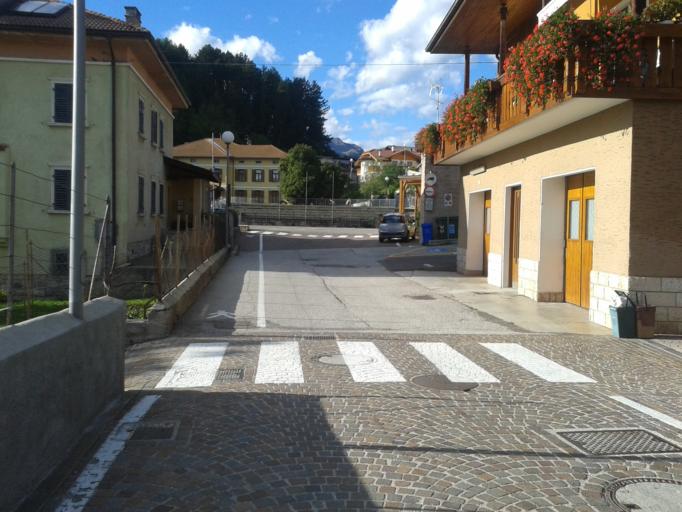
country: IT
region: Trentino-Alto Adige
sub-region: Provincia di Trento
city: Fondo
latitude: 46.4405
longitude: 11.1378
